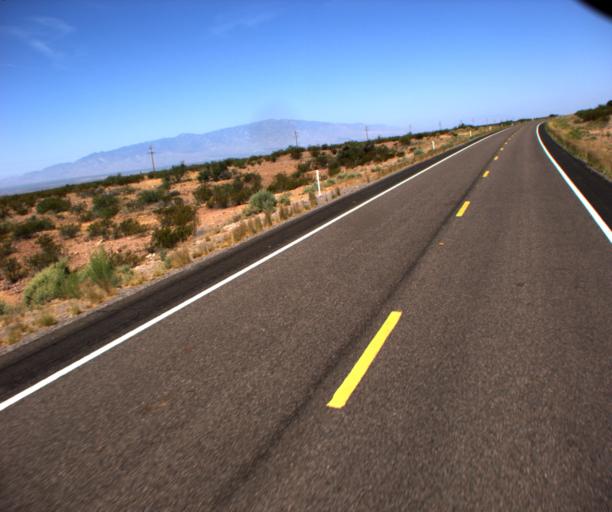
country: US
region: Arizona
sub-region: Graham County
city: Swift Trail Junction
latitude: 32.7540
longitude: -109.4174
